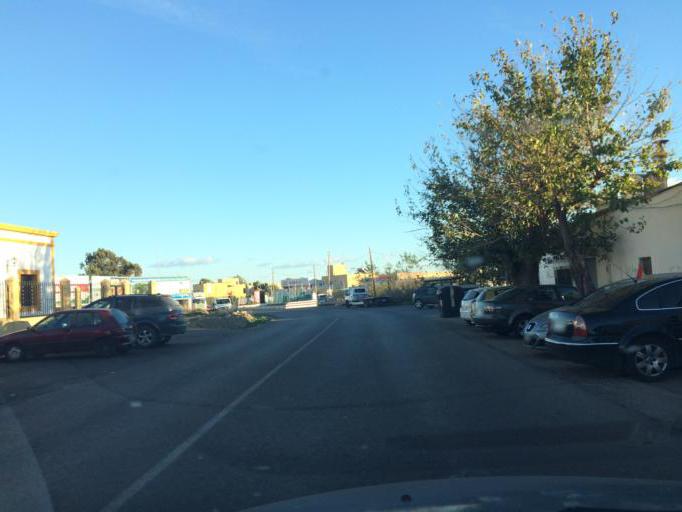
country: ES
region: Andalusia
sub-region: Provincia de Almeria
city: Almeria
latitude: 36.8413
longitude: -2.4251
